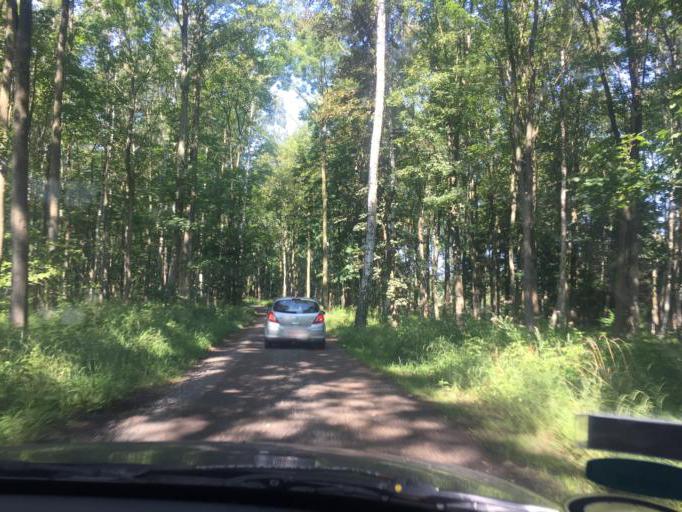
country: DK
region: Zealand
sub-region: Lolland Kommune
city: Maribo
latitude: 54.8172
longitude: 11.5001
